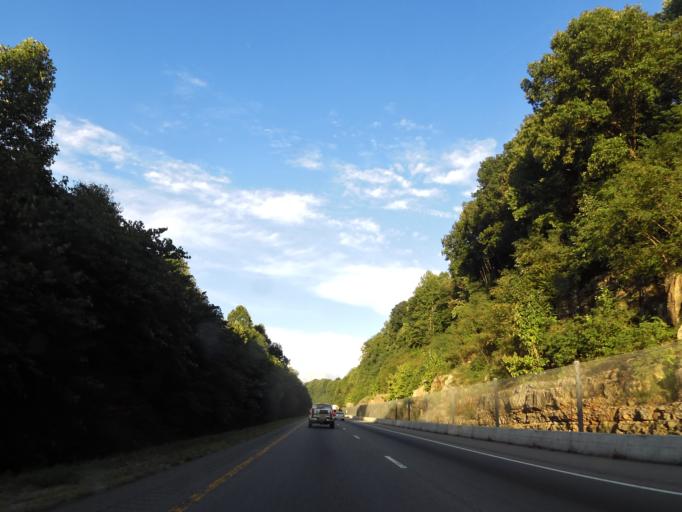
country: US
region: Tennessee
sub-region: Putnam County
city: Algood
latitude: 36.1417
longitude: -85.3877
